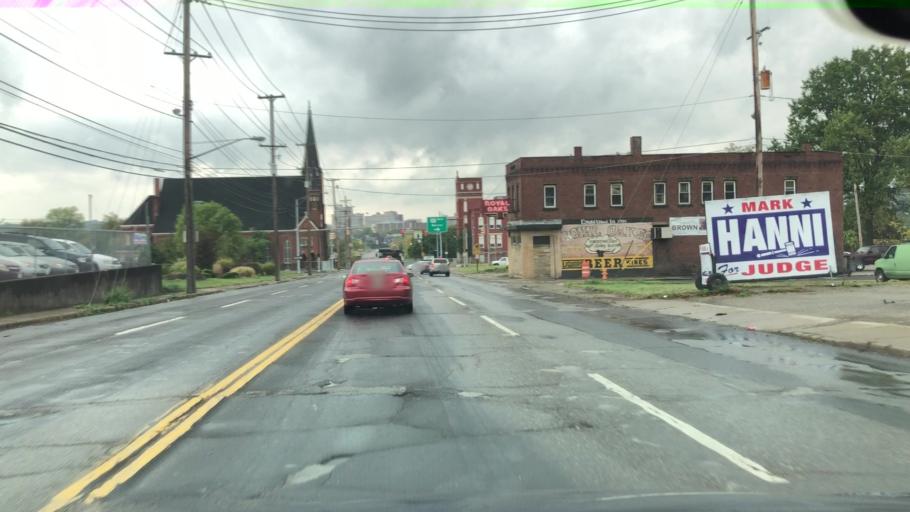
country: US
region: Ohio
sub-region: Mahoning County
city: Youngstown
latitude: 41.1007
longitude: -80.6321
